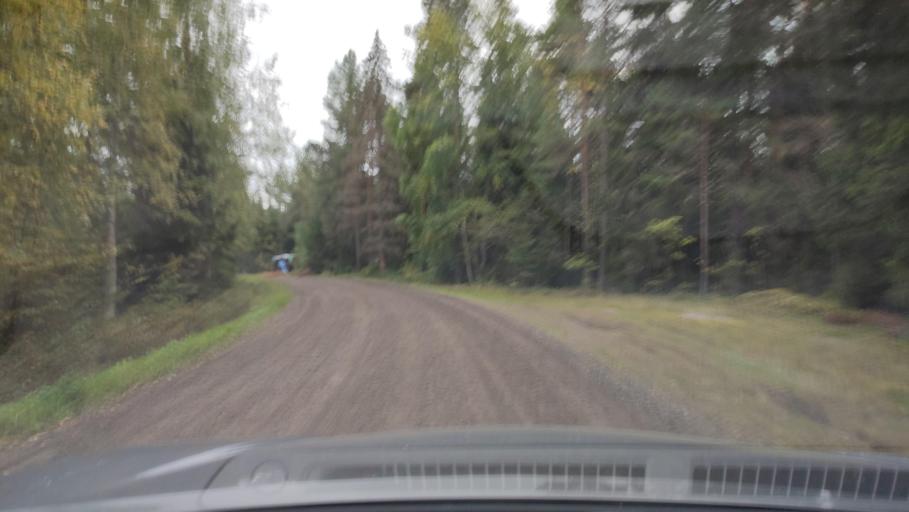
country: FI
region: Southern Ostrobothnia
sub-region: Suupohja
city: Karijoki
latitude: 62.2329
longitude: 21.5709
